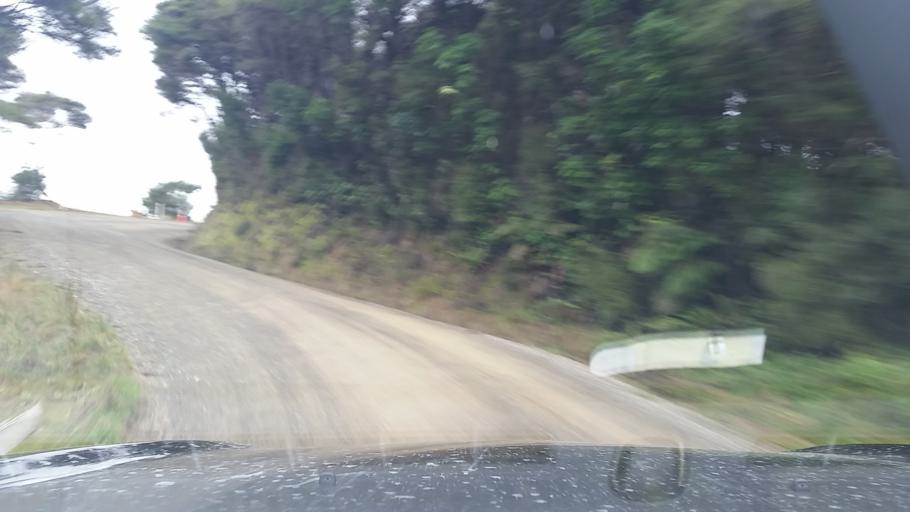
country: NZ
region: Marlborough
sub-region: Marlborough District
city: Picton
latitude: -41.1669
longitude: 174.0114
